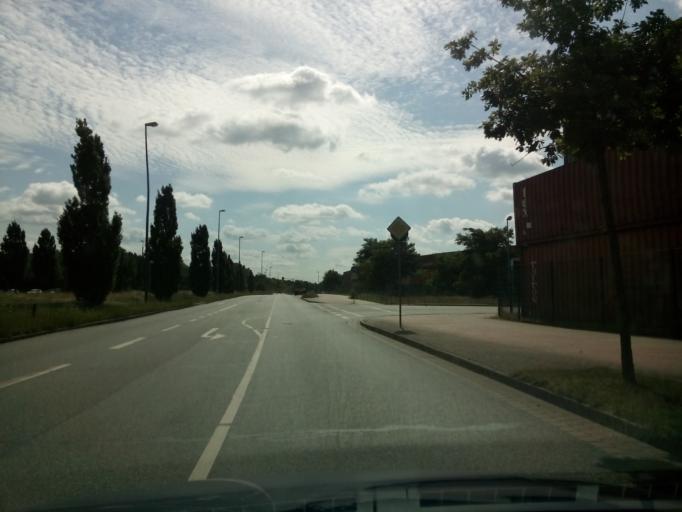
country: DE
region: Lower Saxony
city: Ritterhude
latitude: 53.1247
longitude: 8.7385
